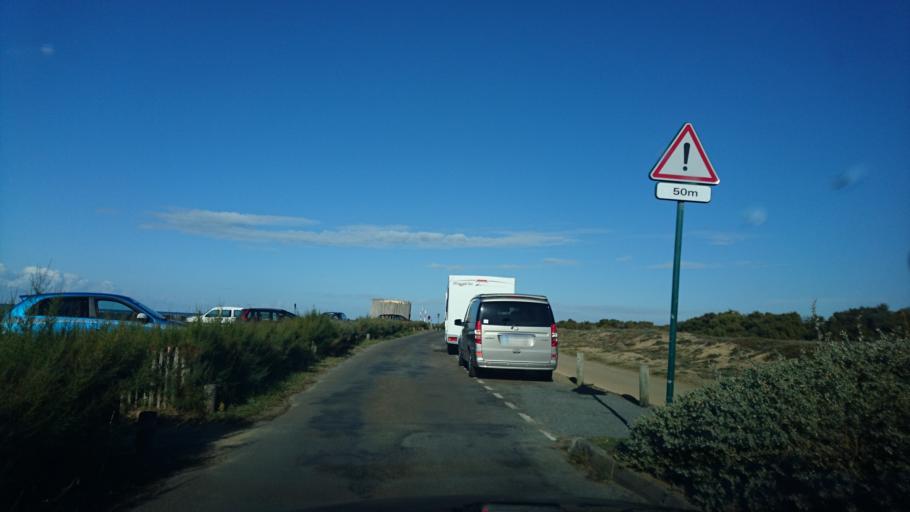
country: FR
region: Pays de la Loire
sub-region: Departement de la Vendee
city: Les Sables-d'Olonne
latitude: 46.5045
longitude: -1.8153
